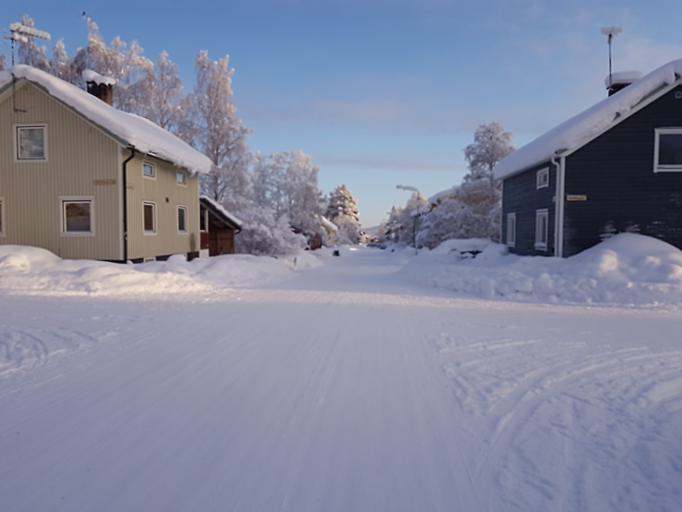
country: SE
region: Norrbotten
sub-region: Jokkmokks Kommun
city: Jokkmokk
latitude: 66.6089
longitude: 19.8160
